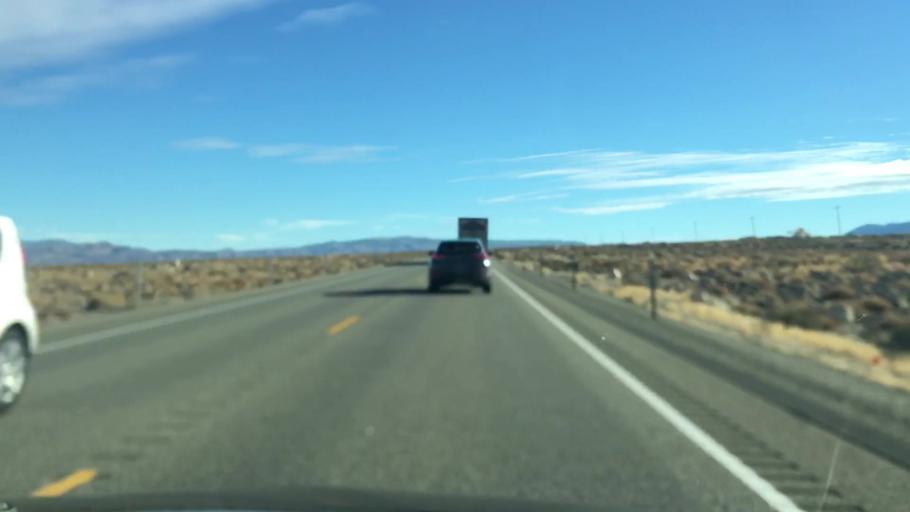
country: US
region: Nevada
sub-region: Mineral County
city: Hawthorne
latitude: 38.5725
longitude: -118.6937
